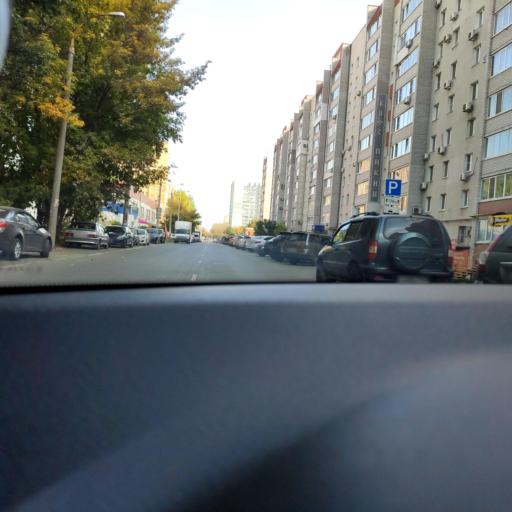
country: RU
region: Samara
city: Samara
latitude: 53.2333
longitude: 50.2501
